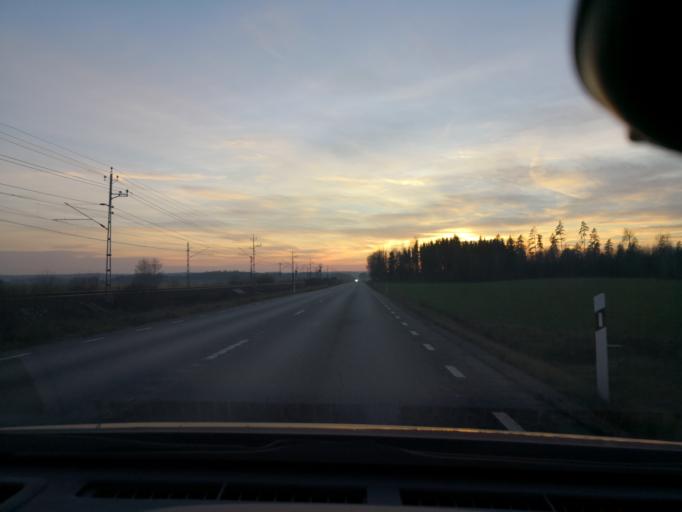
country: SE
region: Vaestmanland
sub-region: Arboga Kommun
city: Arboga
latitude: 59.4278
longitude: 15.9269
